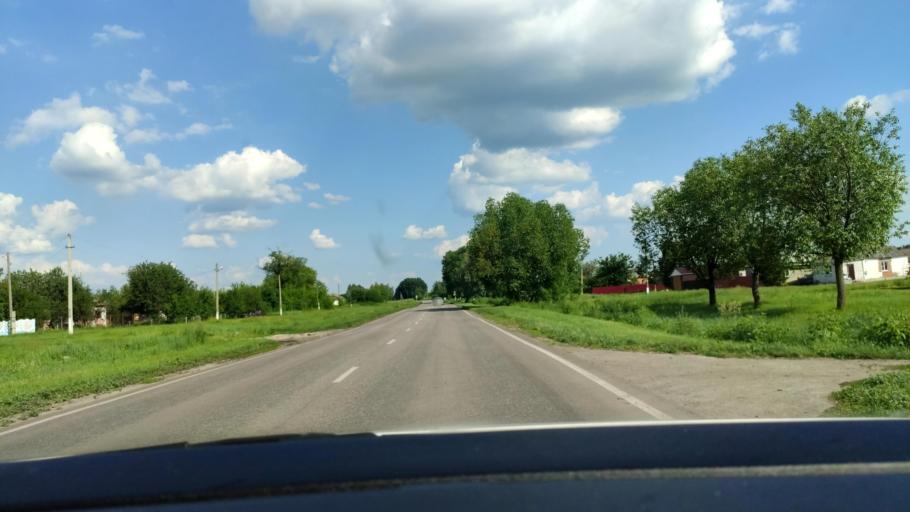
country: RU
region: Voronezj
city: Verkhnyaya Khava
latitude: 51.6703
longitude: 39.9570
